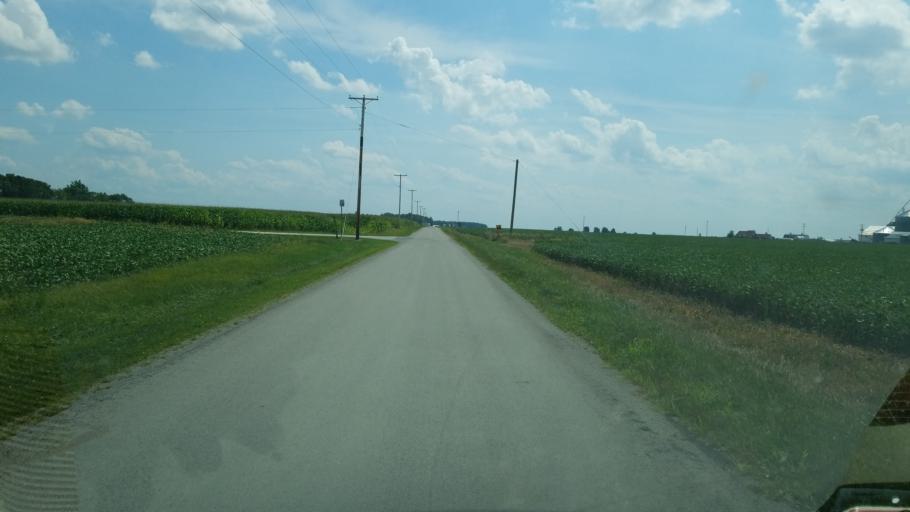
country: US
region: Ohio
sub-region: Hardin County
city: Forest
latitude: 40.7895
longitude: -83.4678
